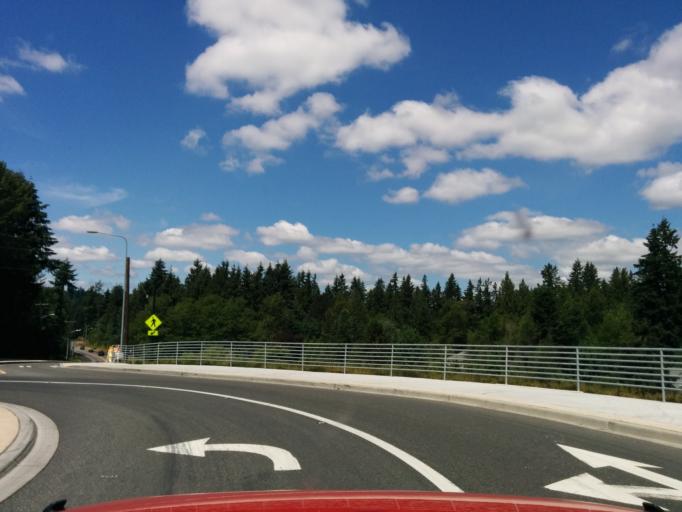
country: US
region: Washington
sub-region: King County
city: Redmond
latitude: 47.6880
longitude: -122.0798
